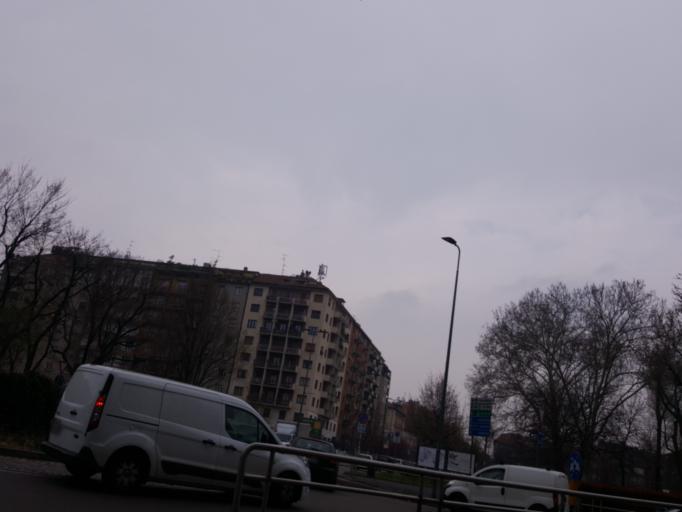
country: IT
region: Lombardy
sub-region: Citta metropolitana di Milano
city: Milano
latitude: 45.4617
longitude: 9.1588
